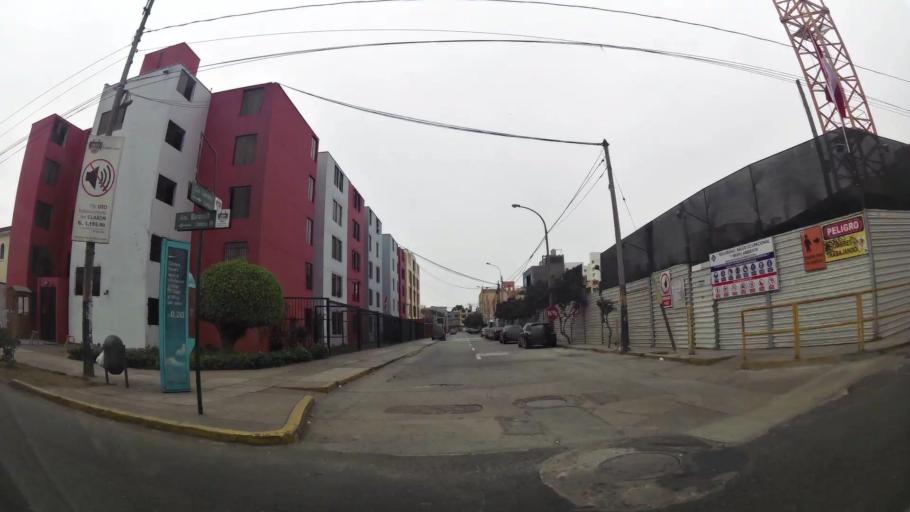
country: PE
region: Lima
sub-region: Lima
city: San Isidro
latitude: -12.0790
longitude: -77.0572
